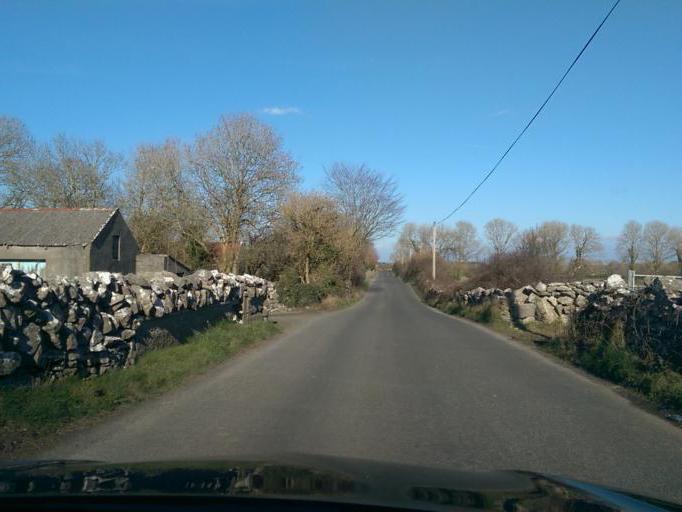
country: IE
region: Connaught
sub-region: County Galway
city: Oranmore
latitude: 53.2271
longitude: -8.8950
